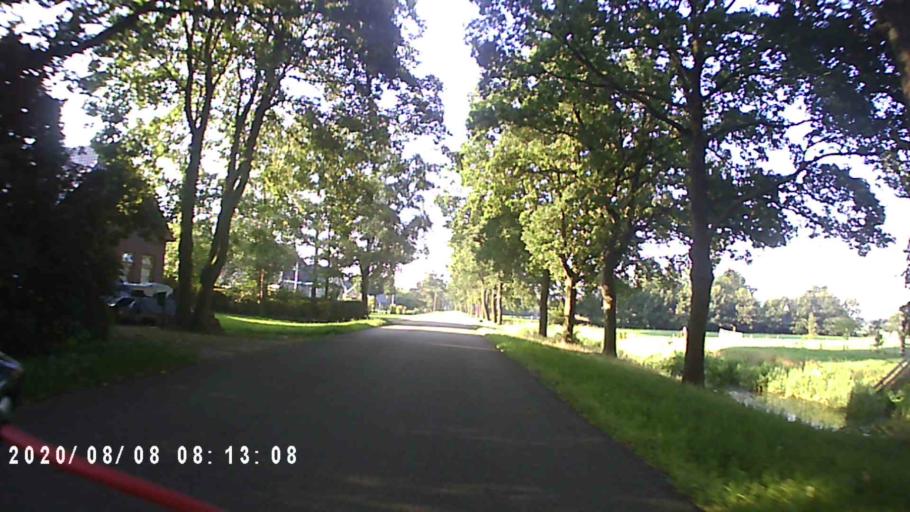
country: NL
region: Groningen
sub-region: Gemeente Leek
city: Leek
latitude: 53.1012
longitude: 6.3400
